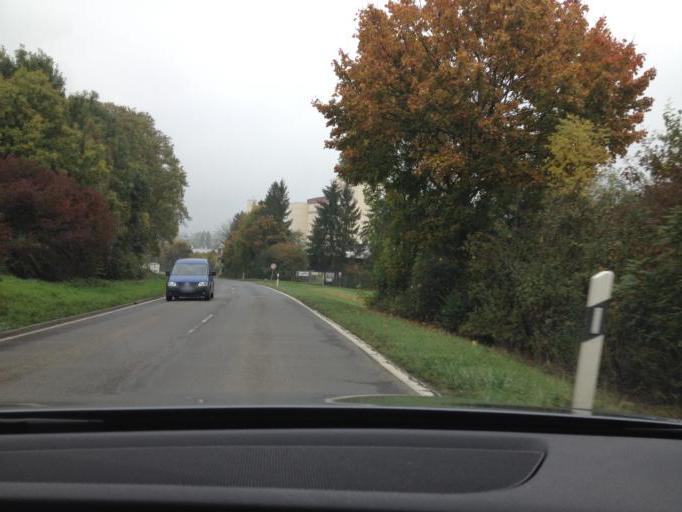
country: DE
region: Baden-Wuerttemberg
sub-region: Regierungsbezirk Stuttgart
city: Untereisesheim
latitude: 49.2244
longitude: 9.1947
